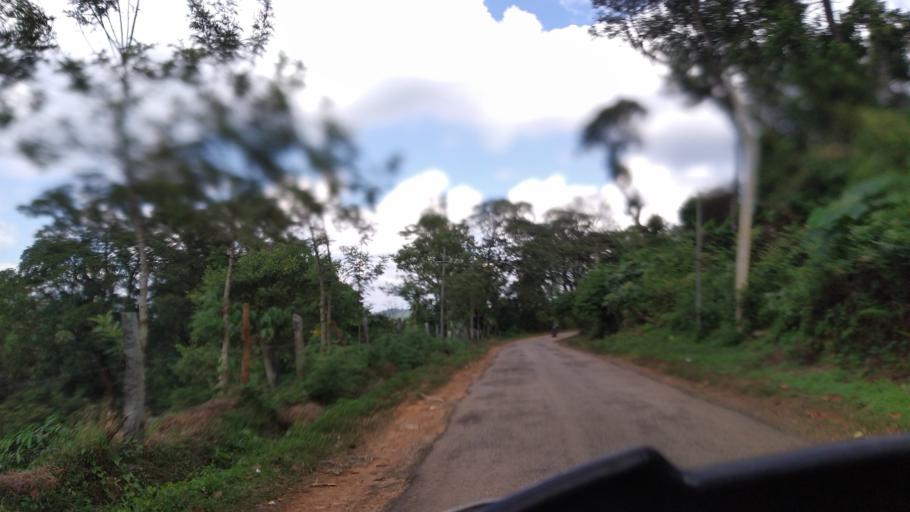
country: IN
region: Karnataka
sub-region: Kodagu
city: Ponnampet
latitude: 12.0361
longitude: 75.9055
